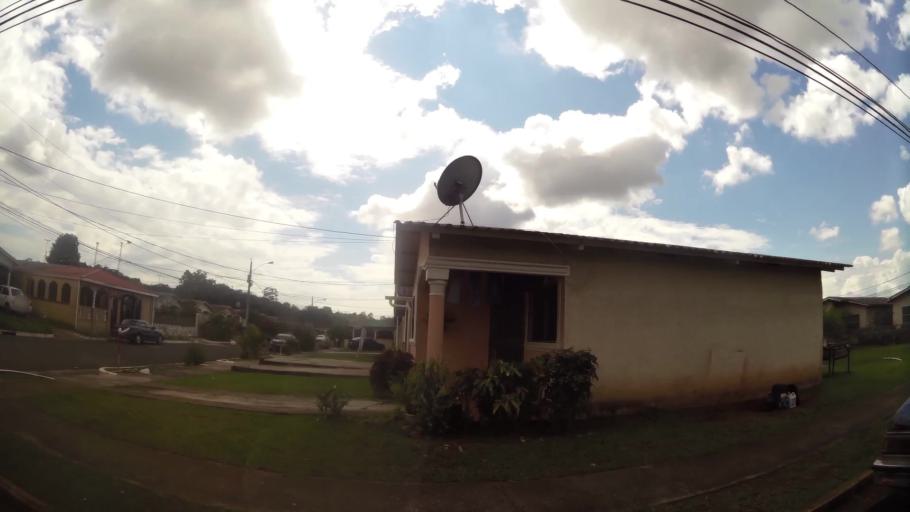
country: PA
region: Panama
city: Nuevo Arraijan
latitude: 8.9347
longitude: -79.7256
